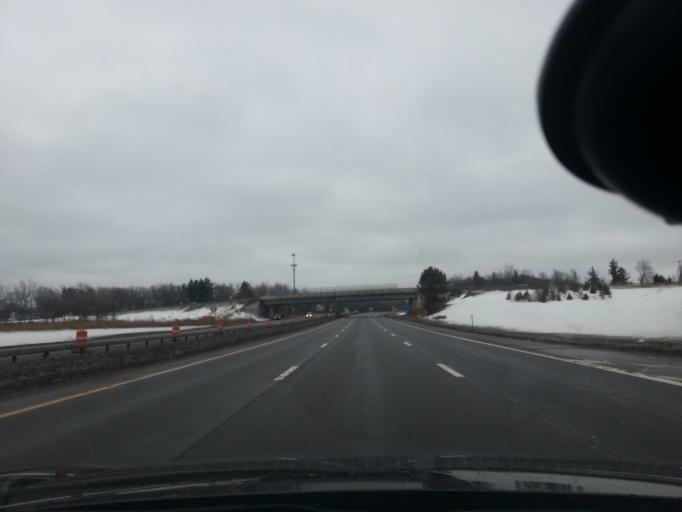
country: US
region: New York
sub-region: Onondaga County
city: Brewerton
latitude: 43.2336
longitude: -76.1295
